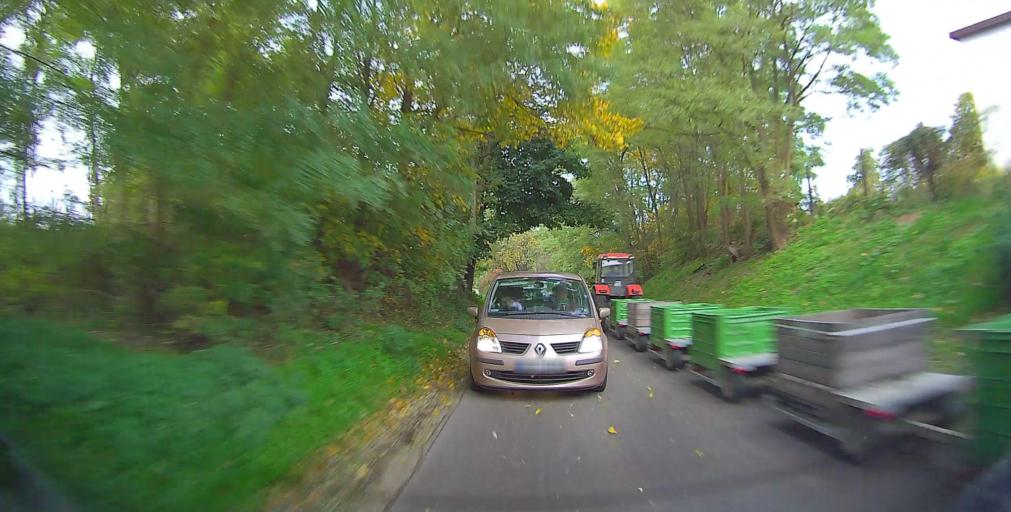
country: PL
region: Masovian Voivodeship
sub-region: Powiat grojecki
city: Mogielnica
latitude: 51.6444
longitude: 20.7382
